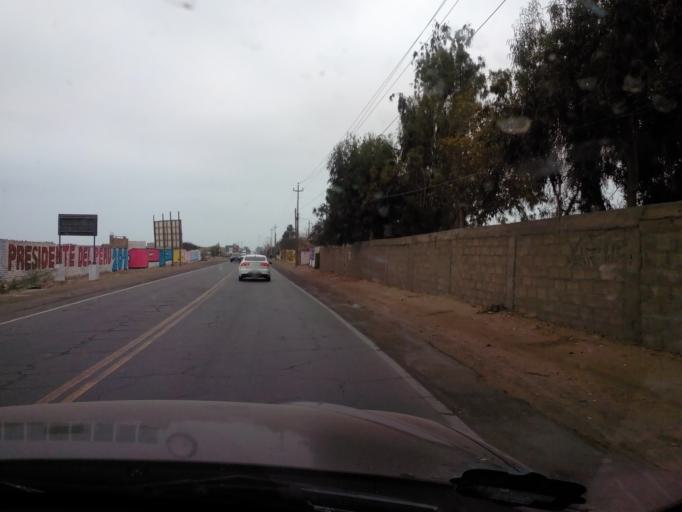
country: PE
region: Ica
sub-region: Provincia de Chincha
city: San Pedro
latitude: -13.4094
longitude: -76.1688
